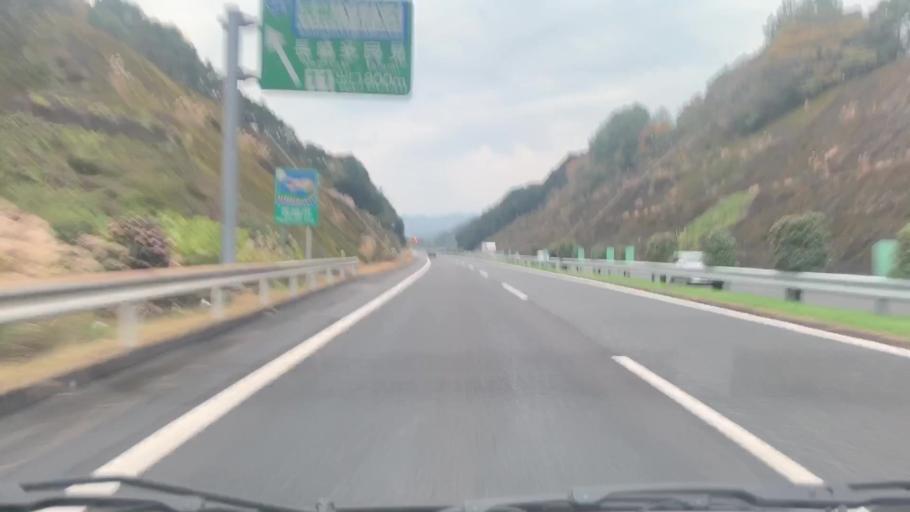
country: JP
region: Nagasaki
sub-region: Isahaya-shi
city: Isahaya
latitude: 32.8182
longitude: 129.9789
